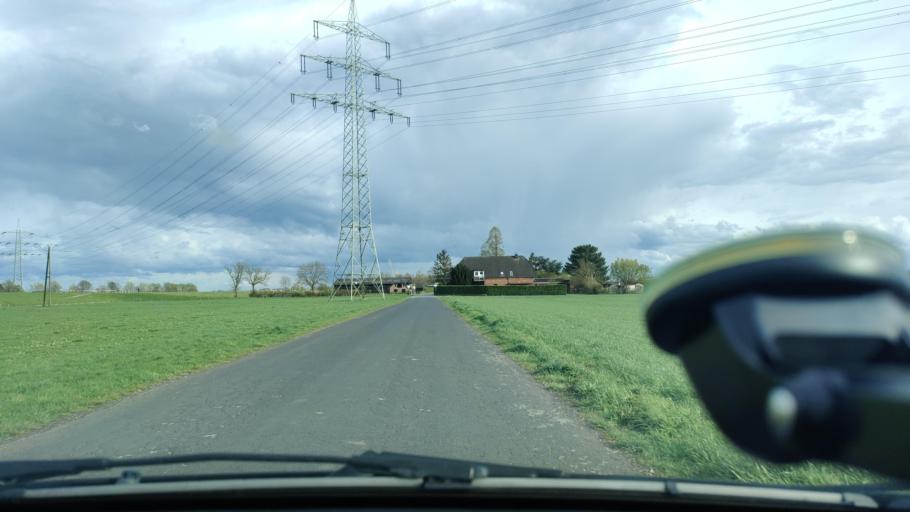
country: DE
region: North Rhine-Westphalia
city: Rees
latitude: 51.7388
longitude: 6.4049
